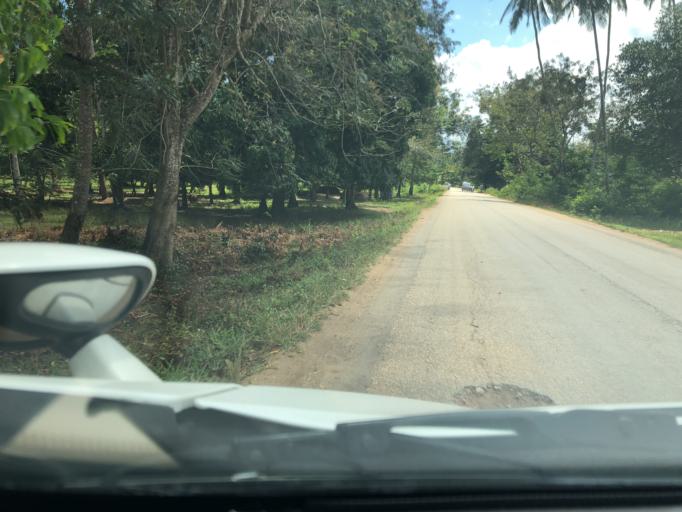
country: TZ
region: Zanzibar Central/South
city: Koani
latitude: -6.0656
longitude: 39.2516
